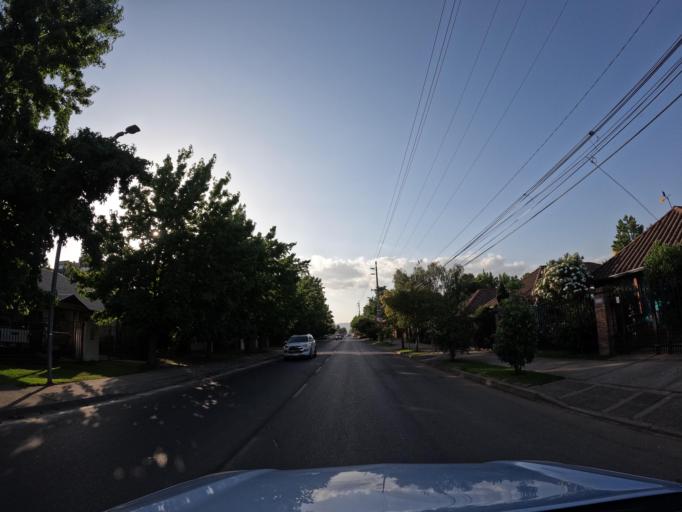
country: CL
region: Maule
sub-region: Provincia de Talca
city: Talca
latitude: -35.4353
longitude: -71.6150
